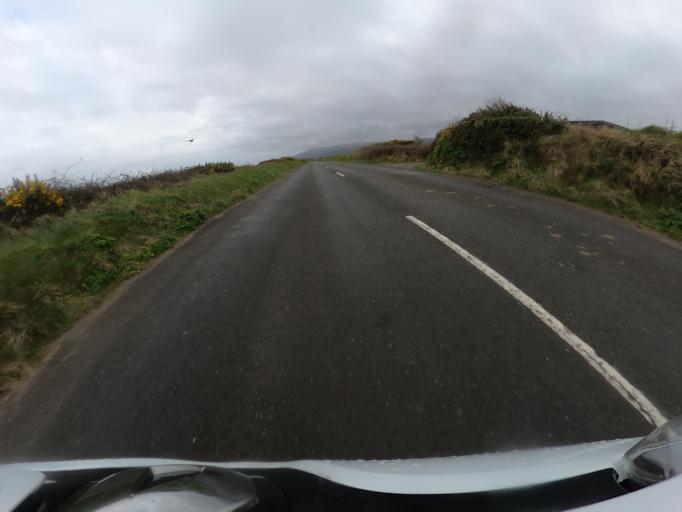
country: IM
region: Ramsey
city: Ramsey
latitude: 54.3555
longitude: -4.5100
